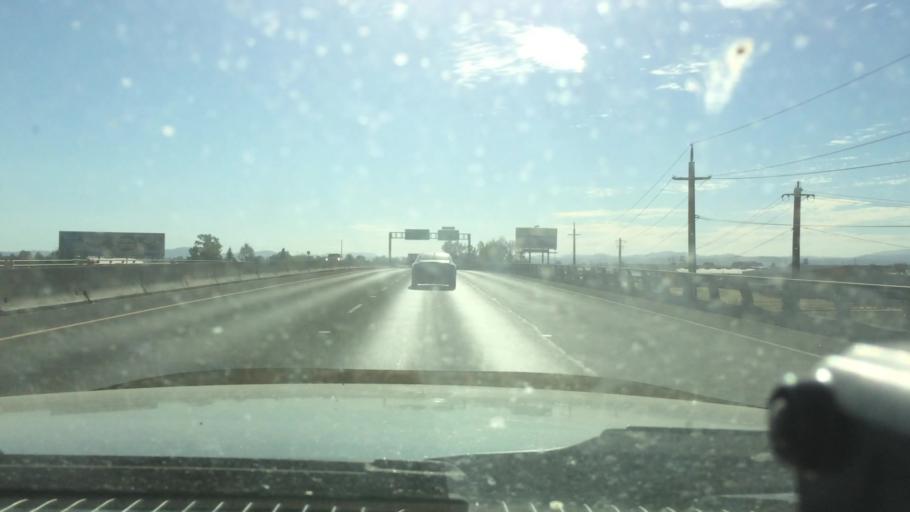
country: US
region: Oregon
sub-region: Lane County
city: Eugene
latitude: 44.0982
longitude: -123.1554
